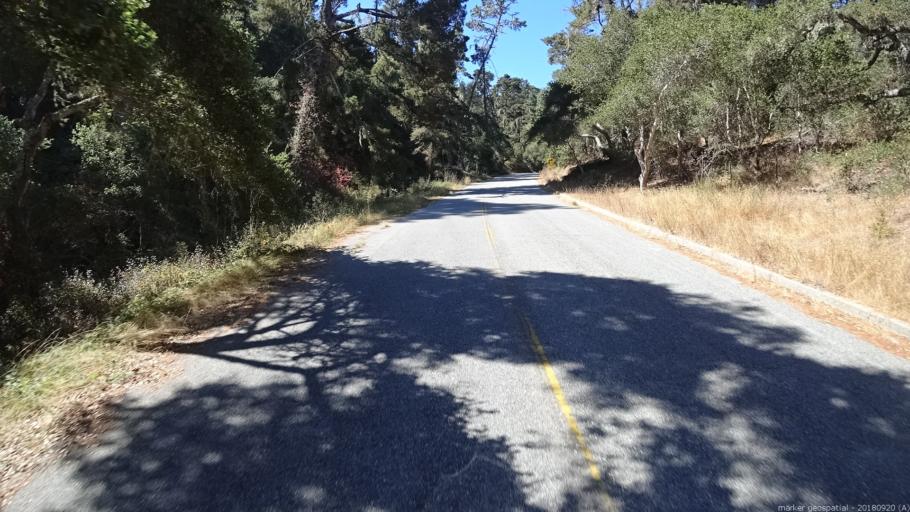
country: US
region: California
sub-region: Monterey County
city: Del Rey Oaks
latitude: 36.5671
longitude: -121.8580
